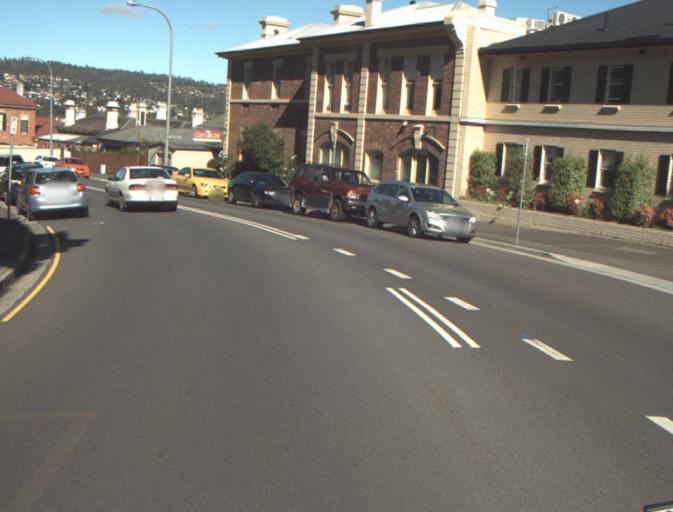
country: AU
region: Tasmania
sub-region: Launceston
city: East Launceston
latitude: -41.4337
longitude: 147.1466
